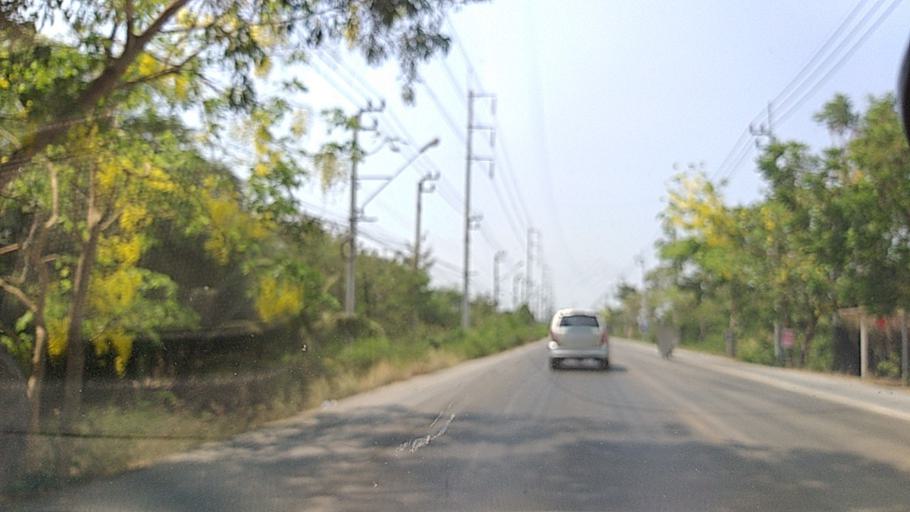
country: TH
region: Nonthaburi
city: Sai Noi
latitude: 13.9493
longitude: 100.3132
